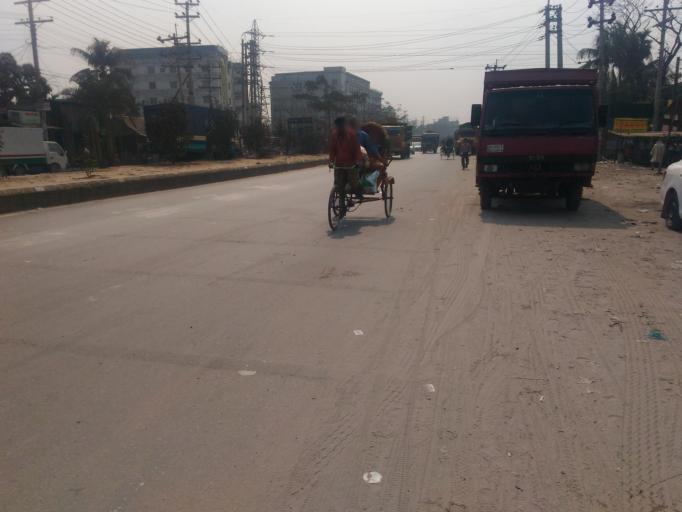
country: BD
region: Dhaka
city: Tungi
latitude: 23.9993
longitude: 90.3826
